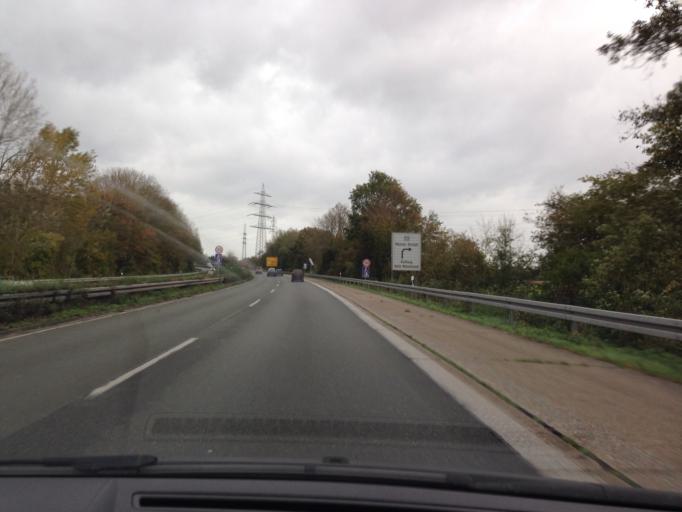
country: DE
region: North Rhine-Westphalia
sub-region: Regierungsbezirk Munster
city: Muenster
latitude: 51.9198
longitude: 7.5897
